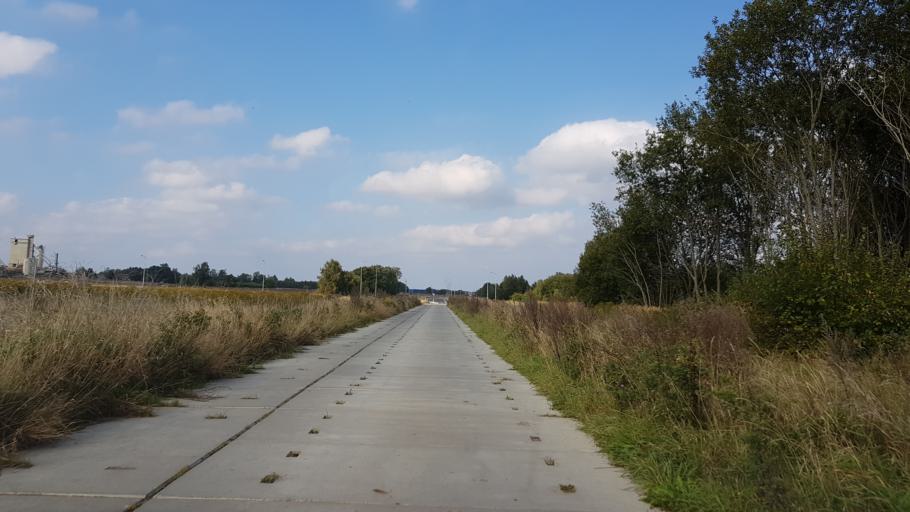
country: PL
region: West Pomeranian Voivodeship
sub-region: Koszalin
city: Koszalin
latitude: 54.1759
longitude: 16.1582
